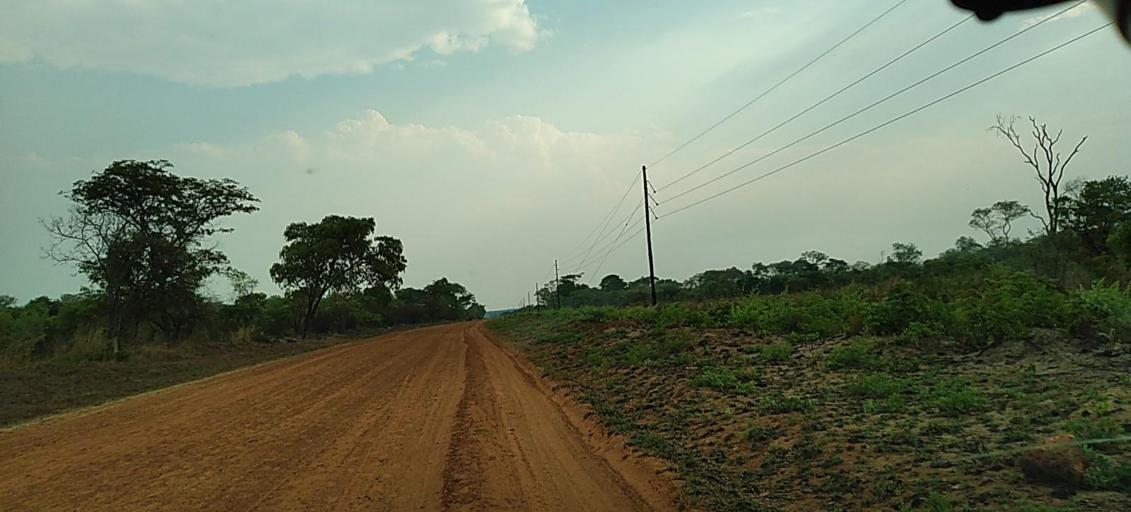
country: ZM
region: Western
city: Lukulu
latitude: -13.9011
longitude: 23.6556
